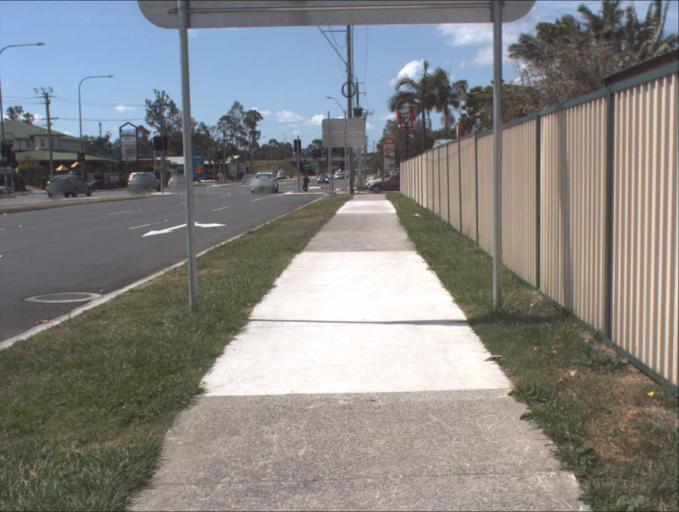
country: AU
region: Queensland
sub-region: Logan
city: Slacks Creek
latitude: -27.6685
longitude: 153.1396
